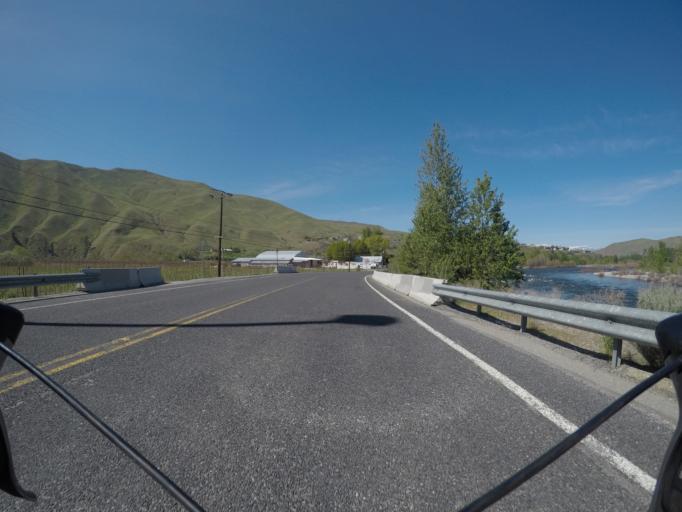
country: US
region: Washington
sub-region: Chelan County
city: West Wenatchee
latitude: 47.4722
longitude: -120.3723
